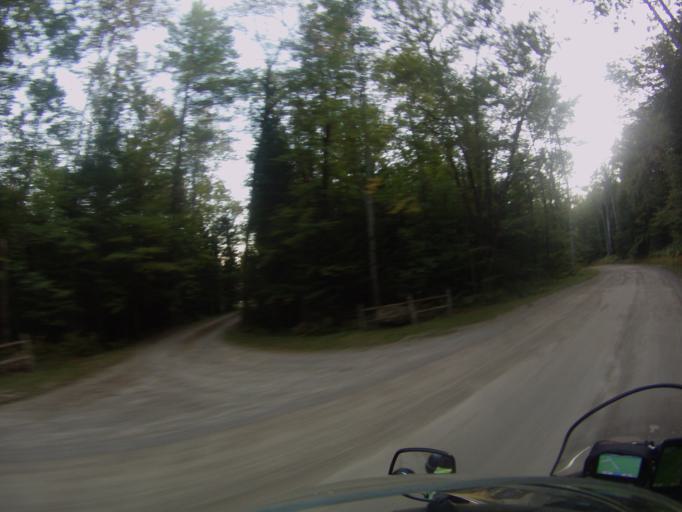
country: US
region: Vermont
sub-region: Addison County
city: Bristol
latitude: 44.0075
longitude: -73.0353
